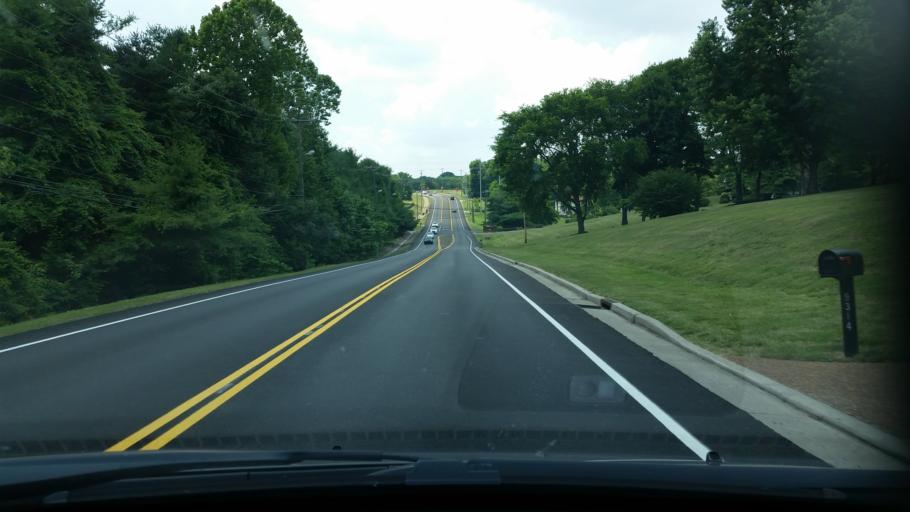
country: US
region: Tennessee
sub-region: Williamson County
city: Brentwood Estates
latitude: 35.9919
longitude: -86.7550
